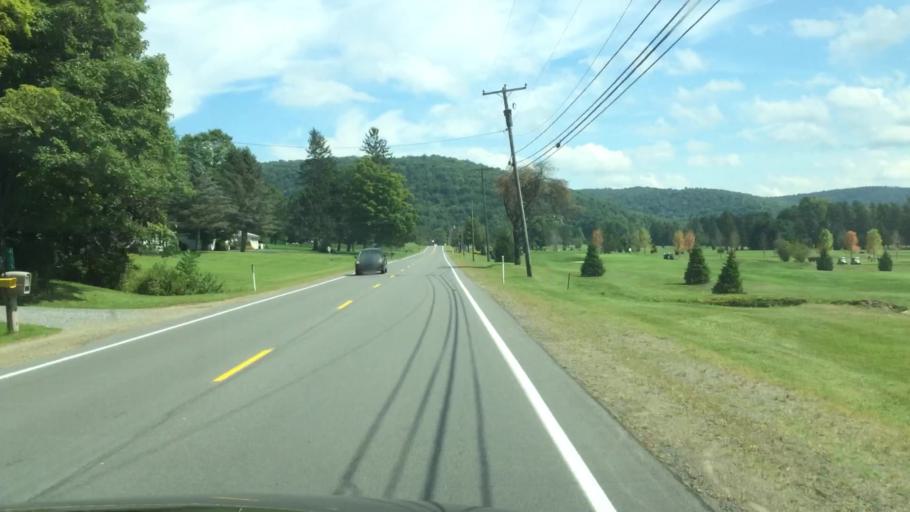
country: US
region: Pennsylvania
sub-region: McKean County
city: Bradford
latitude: 41.9063
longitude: -78.6205
